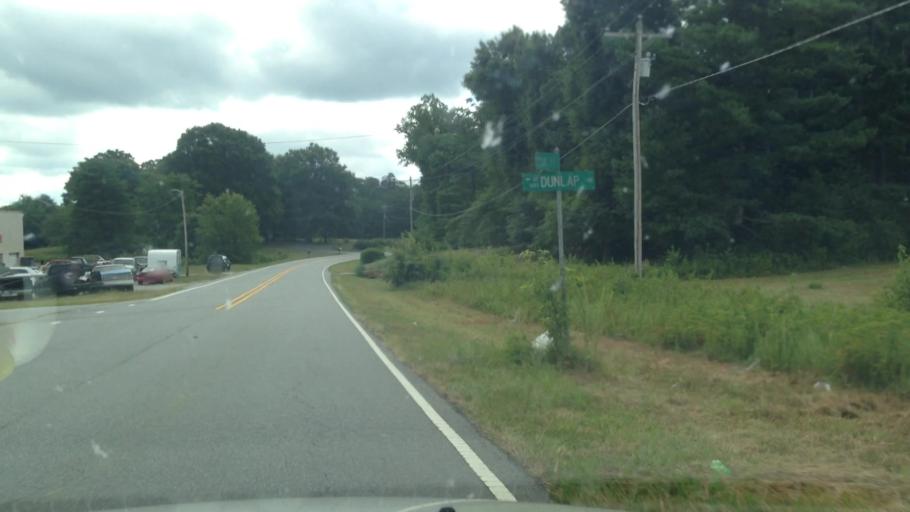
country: US
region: North Carolina
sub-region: Rockingham County
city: Mayodan
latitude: 36.4116
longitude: -80.0570
